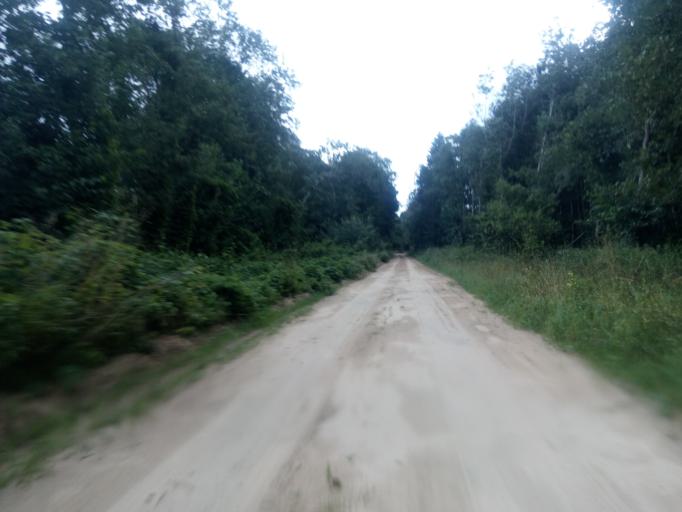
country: BY
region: Vitebsk
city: Dzisna
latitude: 55.7058
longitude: 28.3304
